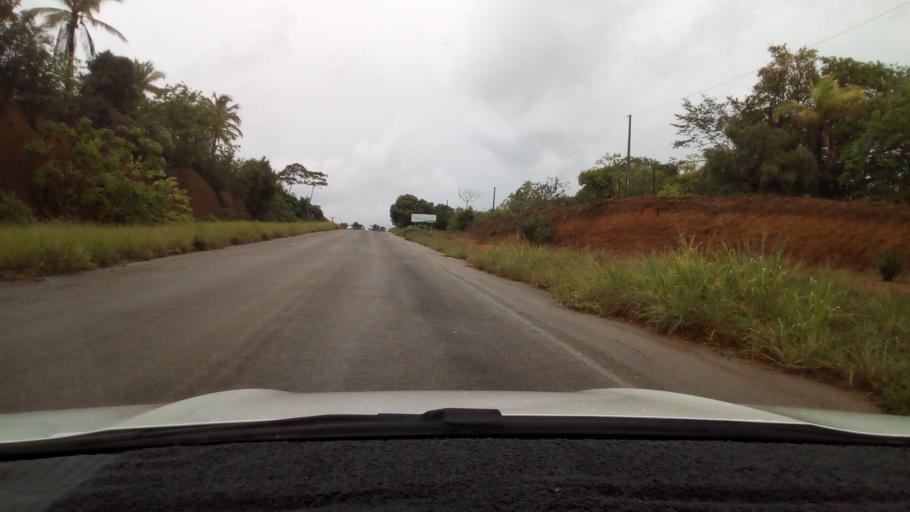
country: BR
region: Paraiba
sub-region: Pitimbu
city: Pitimbu
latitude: -7.4484
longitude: -34.8362
